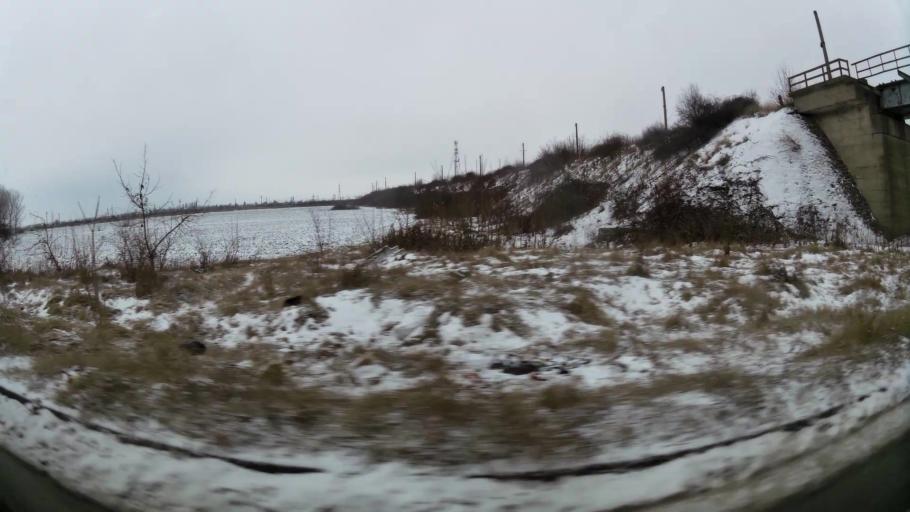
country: RO
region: Prahova
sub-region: Comuna Berceni
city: Corlatesti
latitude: 44.9316
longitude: 26.0605
